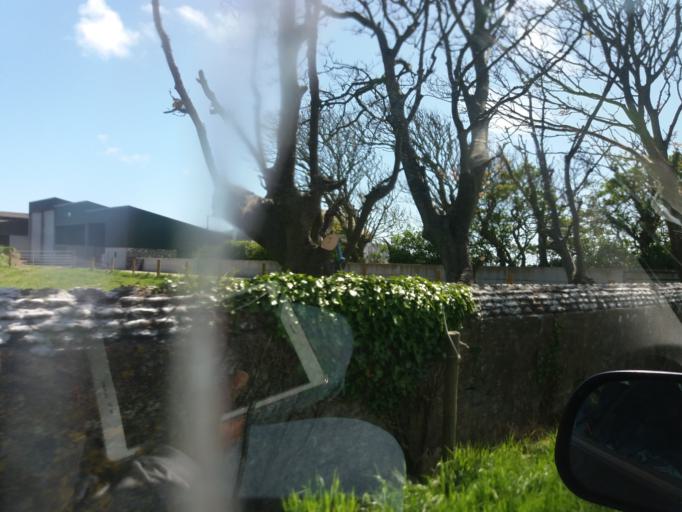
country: IE
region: Munster
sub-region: Waterford
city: Dunmore East
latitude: 52.1458
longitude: -6.9075
